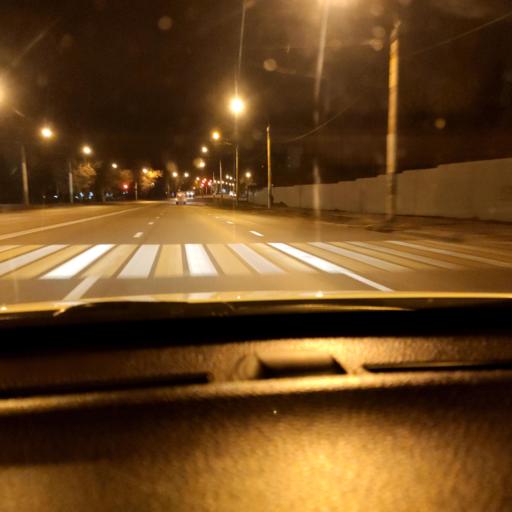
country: RU
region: Voronezj
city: Maslovka
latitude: 51.5997
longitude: 39.2468
